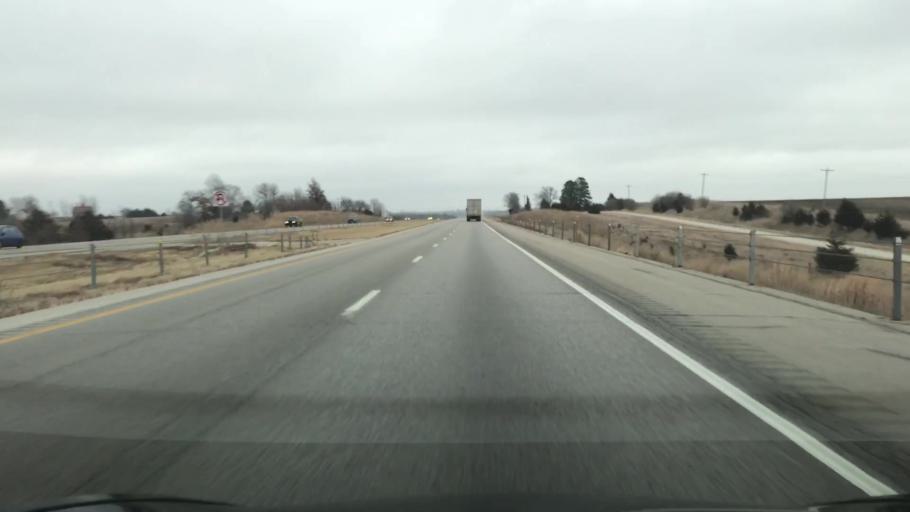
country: US
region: Iowa
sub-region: Madison County
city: Earlham
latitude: 41.5178
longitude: -94.1806
